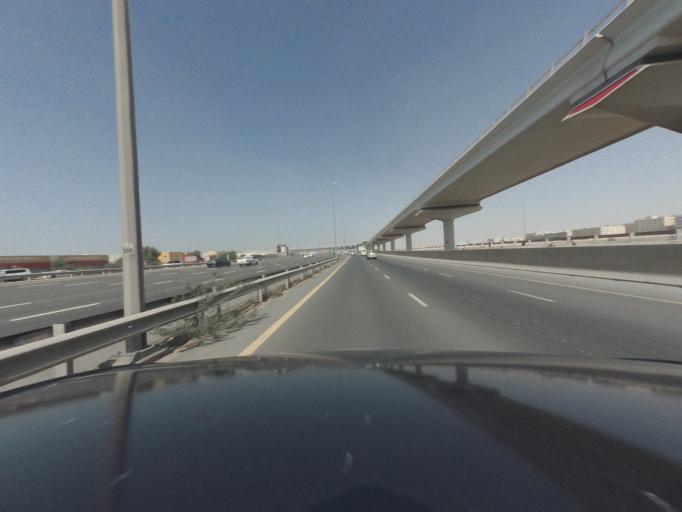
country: AE
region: Dubai
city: Dubai
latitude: 24.9976
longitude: 55.0950
